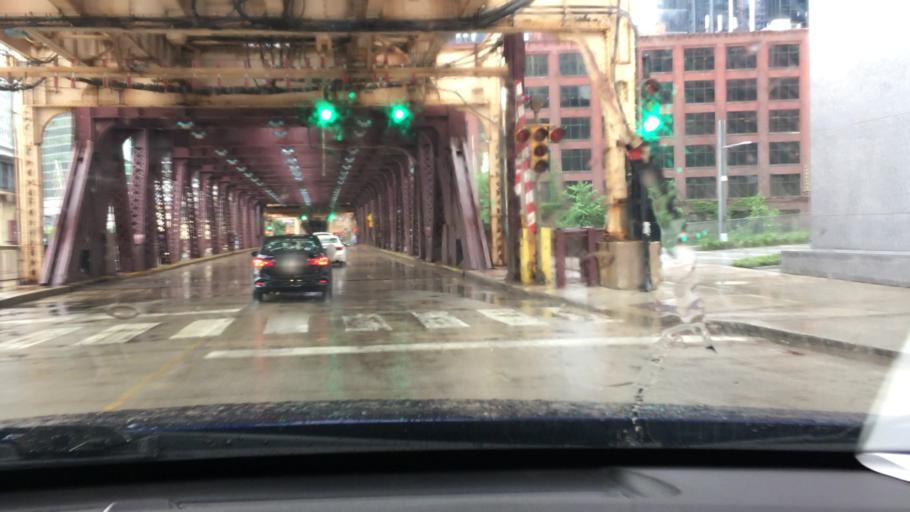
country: US
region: Illinois
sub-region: Cook County
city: Chicago
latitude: 41.8857
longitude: -87.6388
